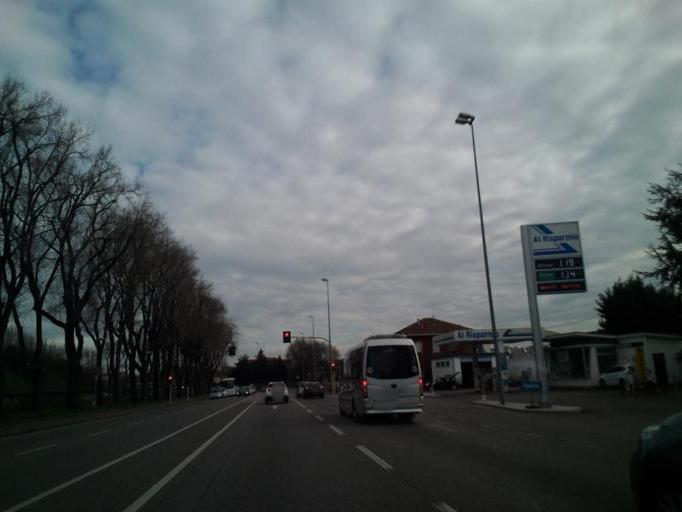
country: IT
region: Veneto
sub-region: Provincia di Verona
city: Verona
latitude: 45.4346
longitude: 11.0072
